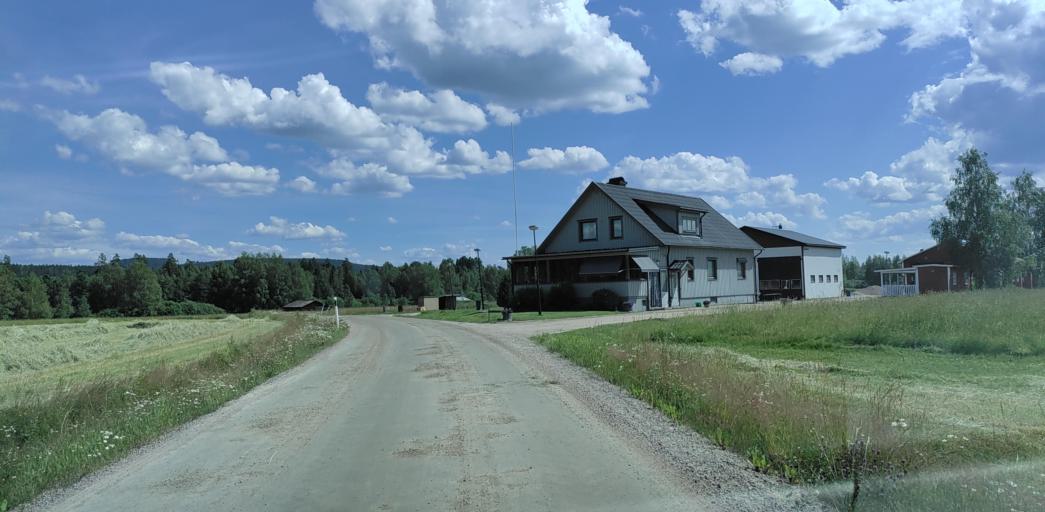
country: SE
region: Vaermland
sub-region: Hagfors Kommun
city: Ekshaerad
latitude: 60.1300
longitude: 13.4660
